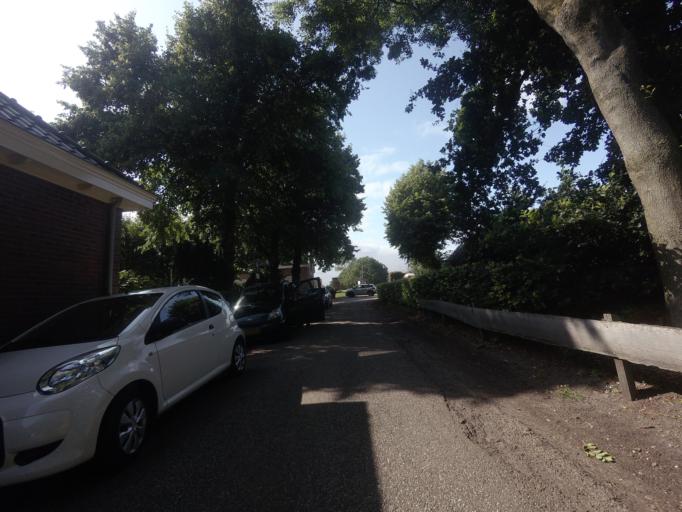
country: NL
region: North Holland
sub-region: Gemeente Haarlem
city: Haarlem
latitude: 52.4042
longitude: 4.6948
